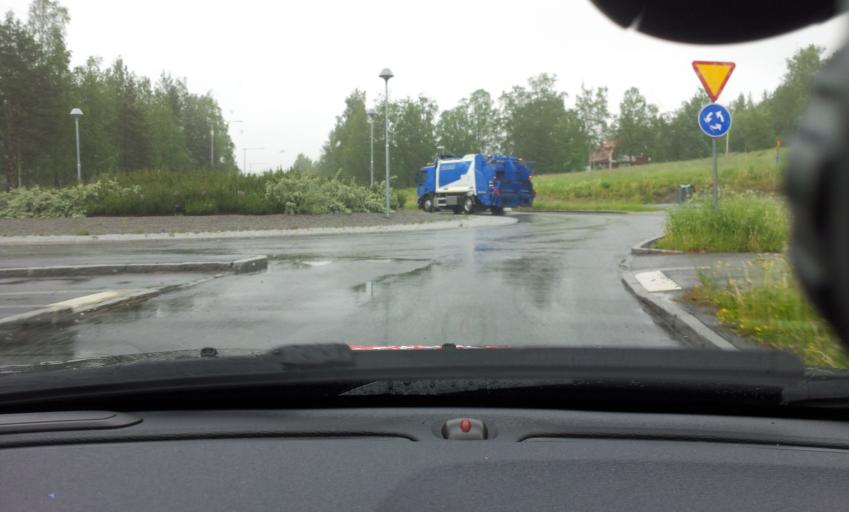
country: SE
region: Jaemtland
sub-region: OEstersunds Kommun
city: Ostersund
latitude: 63.1940
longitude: 14.6621
